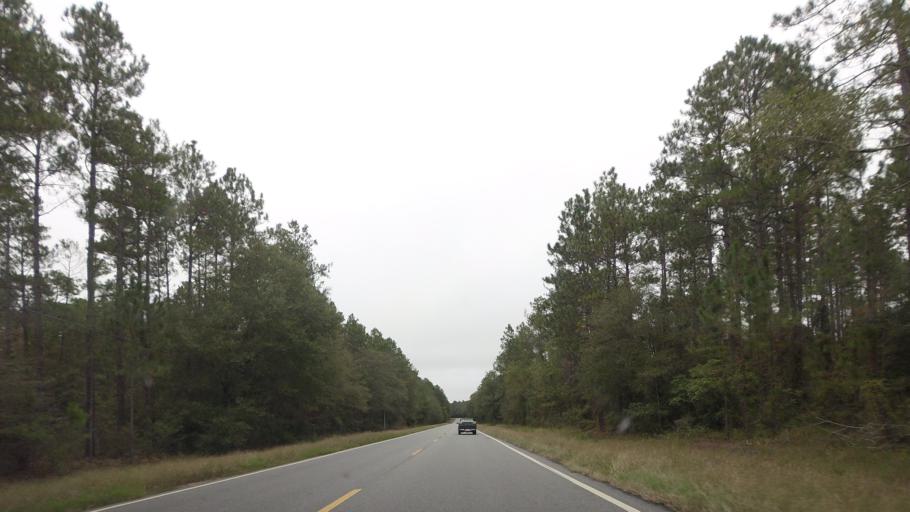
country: US
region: Georgia
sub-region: Berrien County
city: Enigma
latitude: 31.4134
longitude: -83.2428
